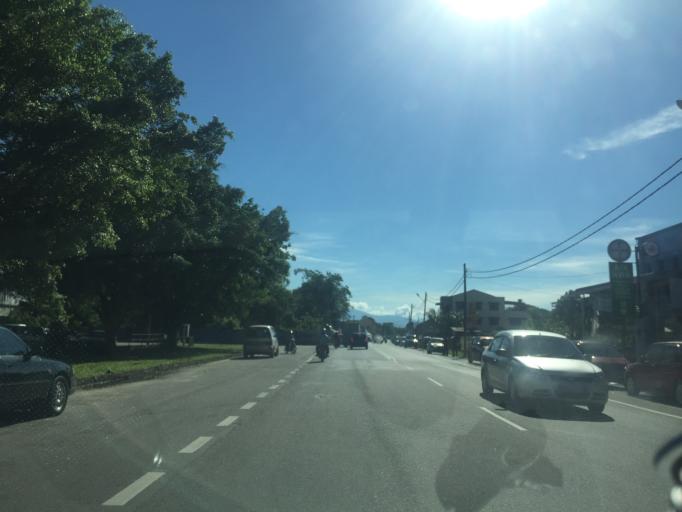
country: MY
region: Penang
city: Tasek Glugor
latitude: 5.5141
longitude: 100.5511
